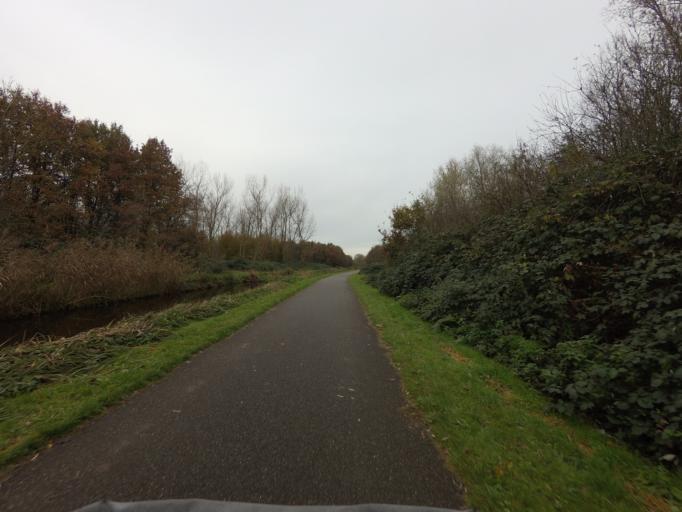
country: NL
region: North Holland
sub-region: Gemeente Amsterdam
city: Driemond
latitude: 52.3232
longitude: 4.9990
